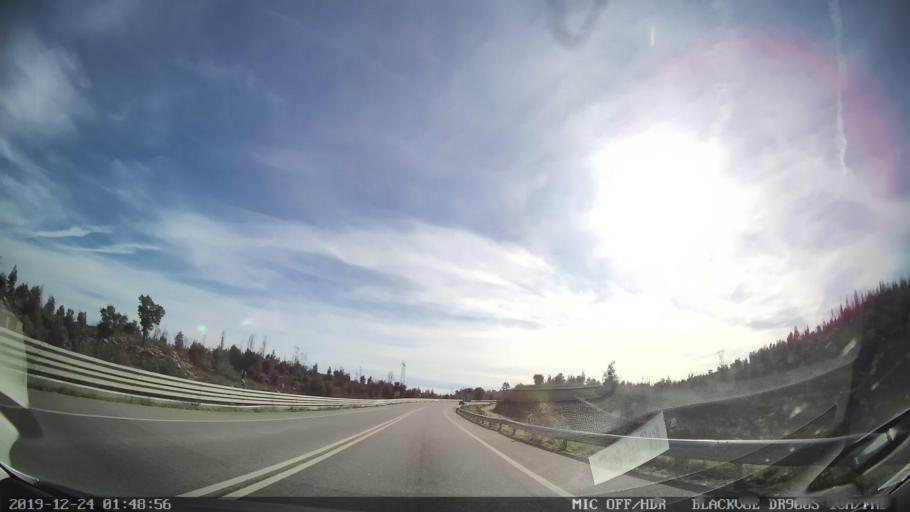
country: PT
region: Portalegre
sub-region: Nisa
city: Nisa
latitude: 39.5171
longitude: -7.7706
